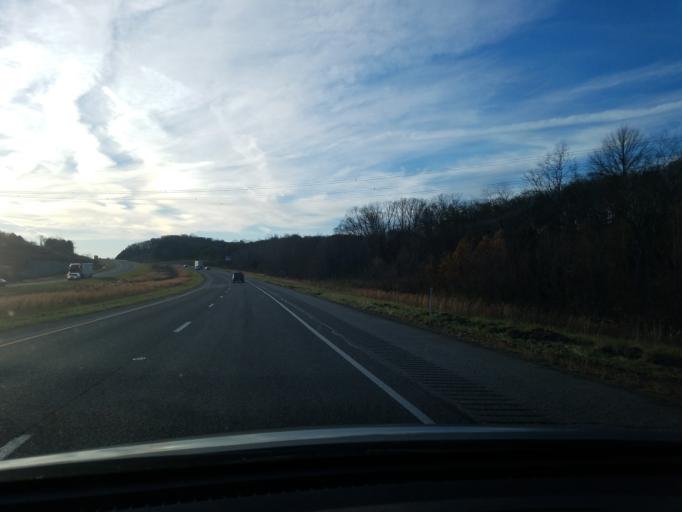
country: US
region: Indiana
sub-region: Dubois County
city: Ferdinand
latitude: 38.2164
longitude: -86.7363
